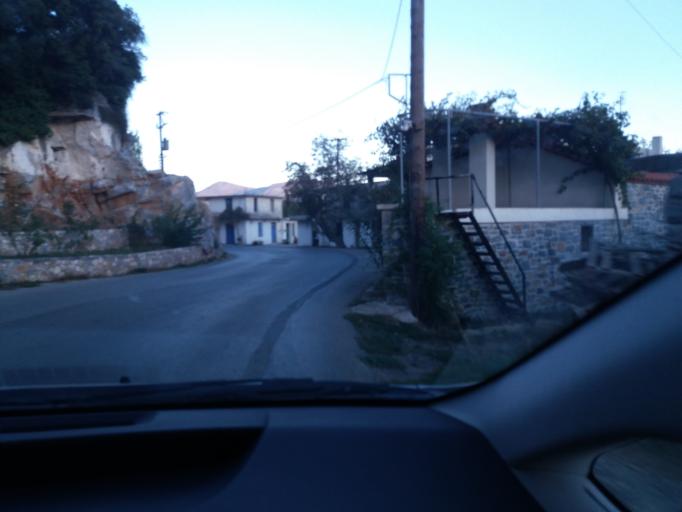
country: GR
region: Crete
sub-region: Nomos Irakleiou
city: Mokhos
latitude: 35.1968
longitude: 25.4643
